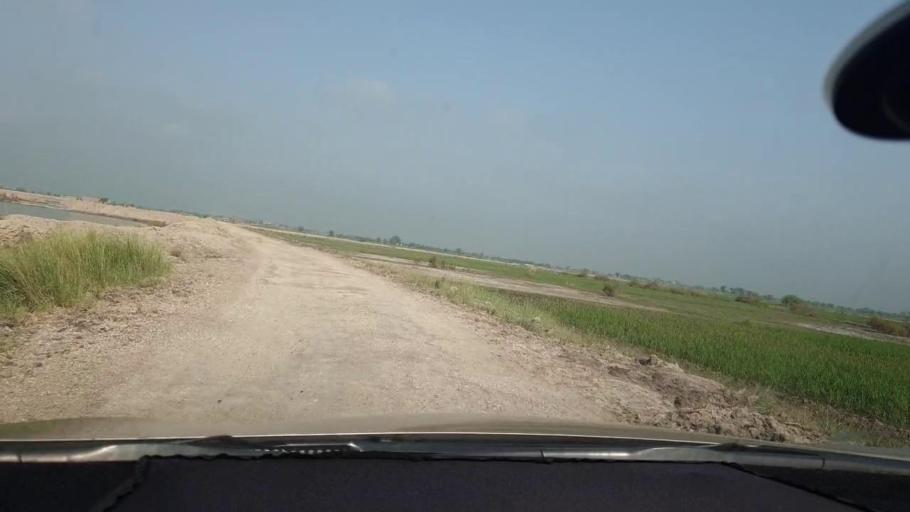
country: PK
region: Sindh
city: Kambar
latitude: 27.5355
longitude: 68.0623
